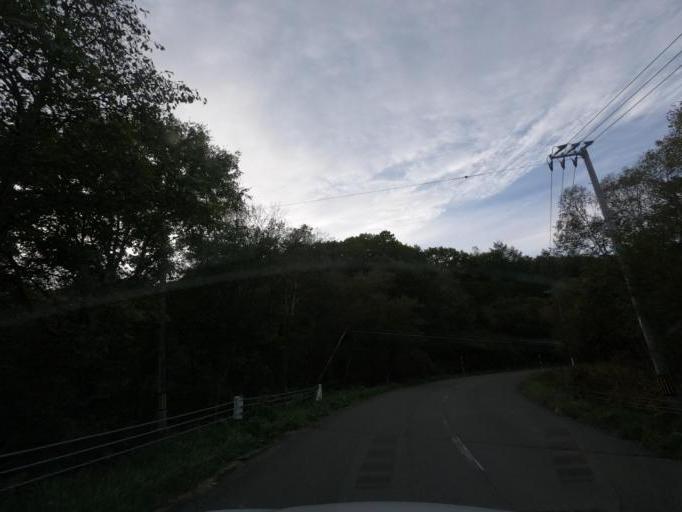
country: JP
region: Hokkaido
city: Obihiro
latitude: 42.5449
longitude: 143.3964
